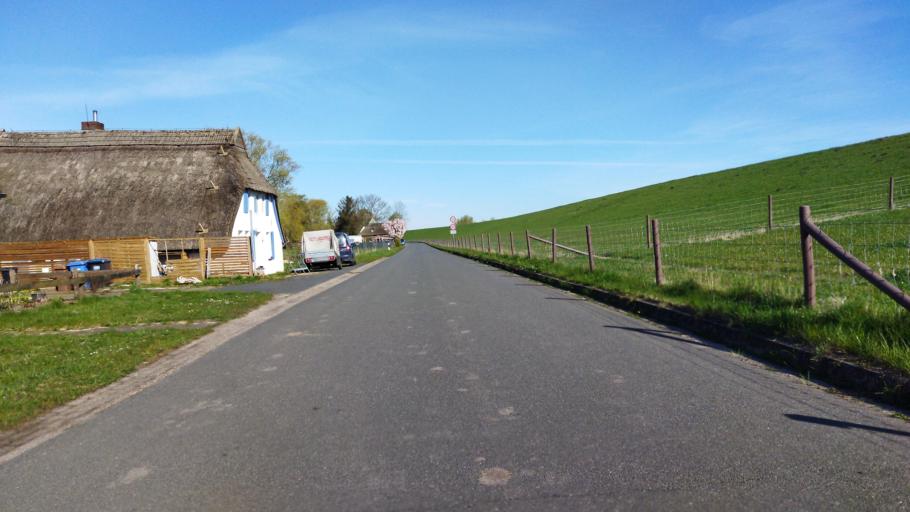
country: DE
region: Lower Saxony
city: Elsfleth
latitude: 53.2097
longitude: 8.4839
